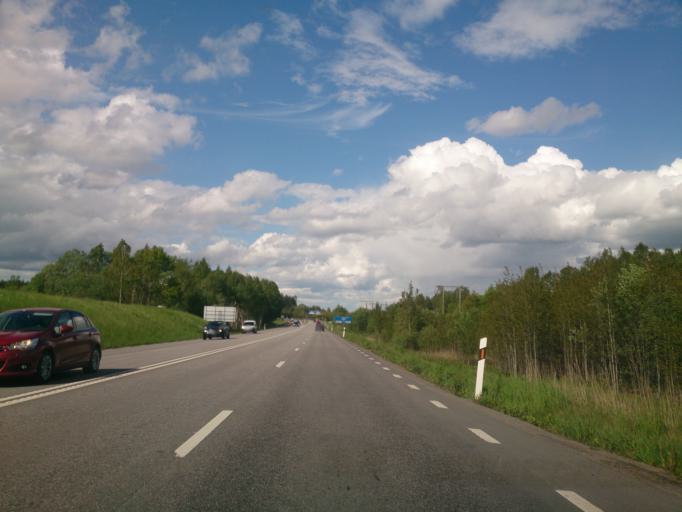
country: SE
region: OEstergoetland
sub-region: Linkopings Kommun
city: Malmslatt
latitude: 58.3954
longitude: 15.5483
